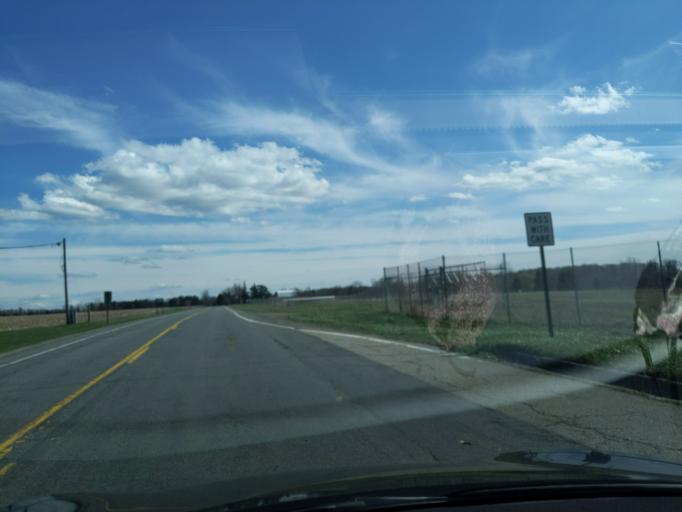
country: US
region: Michigan
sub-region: Ingham County
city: Mason
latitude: 42.5672
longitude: -84.4138
